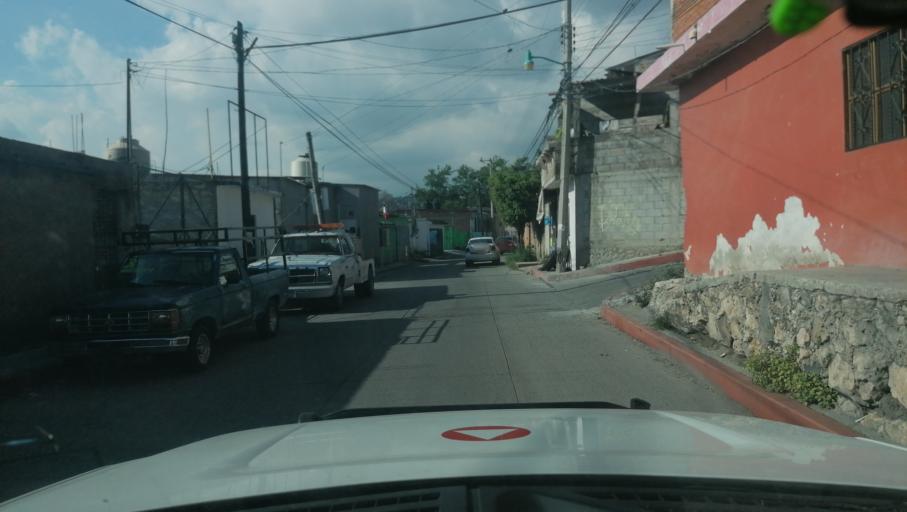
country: MX
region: Morelos
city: Emiliano Zapata
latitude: 18.8395
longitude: -99.1933
